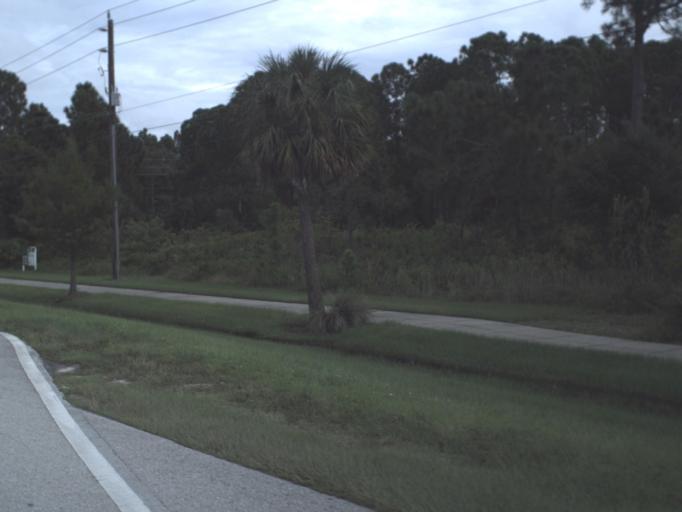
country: US
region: Florida
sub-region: Sarasota County
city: North Port
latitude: 27.0675
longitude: -82.1570
